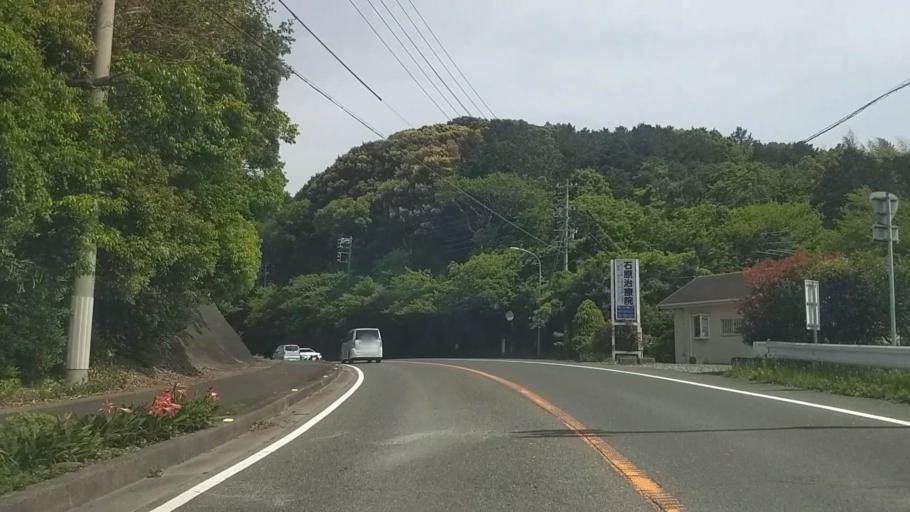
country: JP
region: Shizuoka
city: Kosai-shi
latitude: 34.7886
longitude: 137.6088
